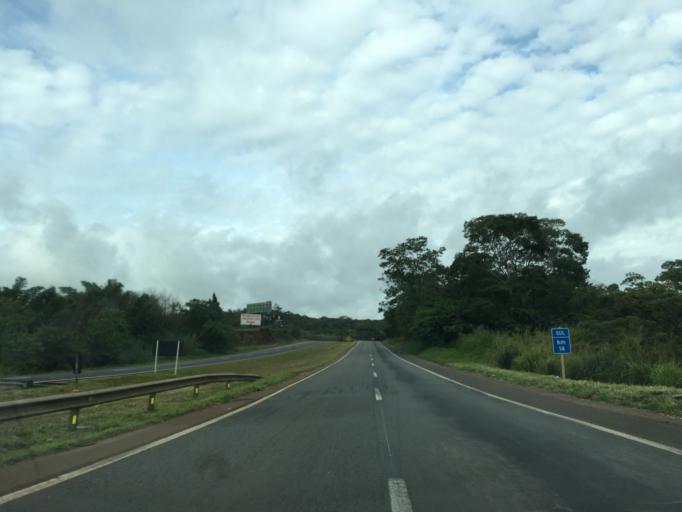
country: BR
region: Goias
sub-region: Abadiania
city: Abadiania
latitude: -16.1109
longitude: -48.3514
